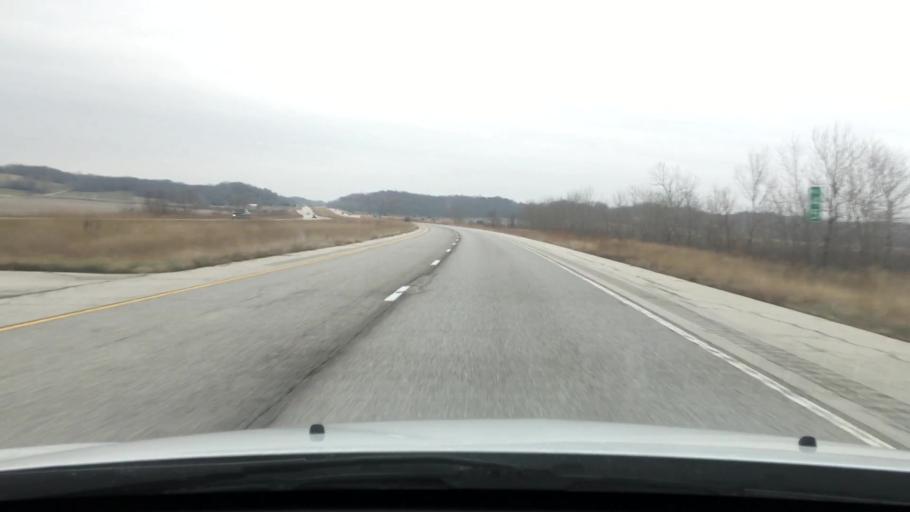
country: US
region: Illinois
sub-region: Pike County
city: Griggsville
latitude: 39.6853
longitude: -90.5872
